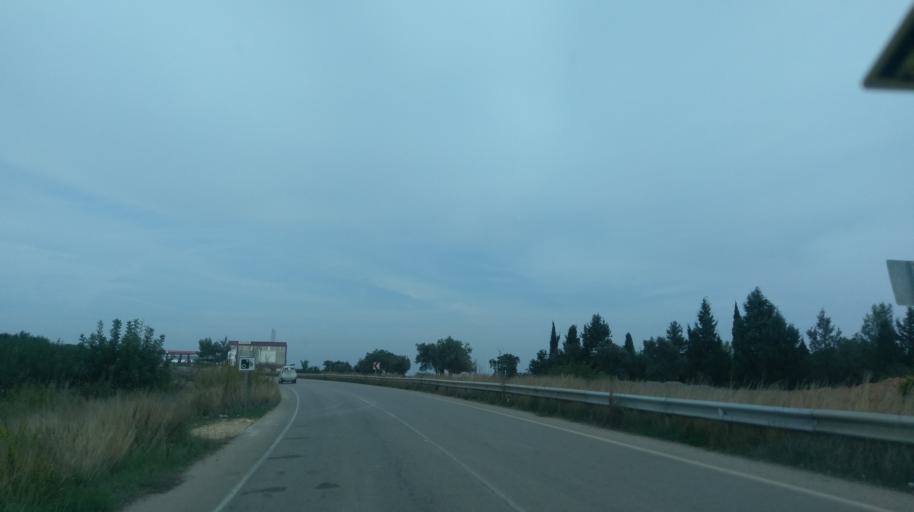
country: CY
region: Ammochostos
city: Leonarisso
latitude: 35.4193
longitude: 34.1242
